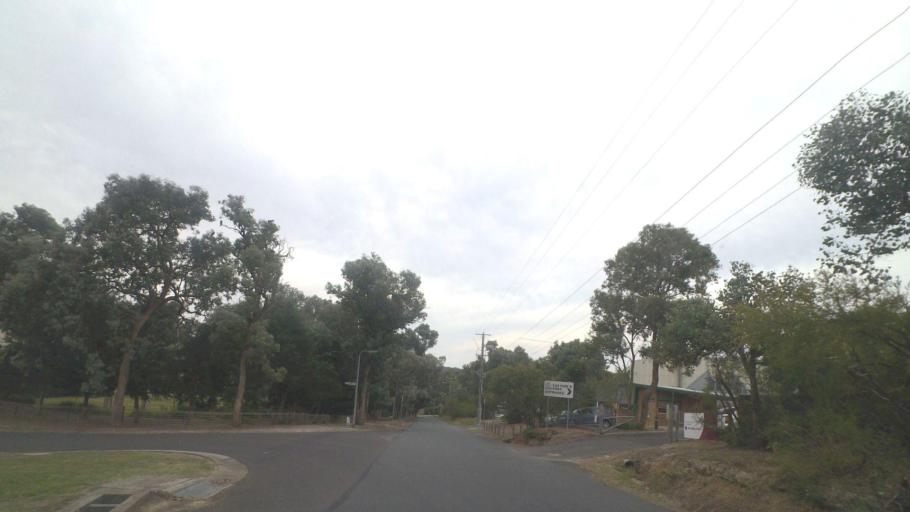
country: AU
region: Victoria
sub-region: Nillumbik
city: Eltham
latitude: -37.7471
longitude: 145.1838
